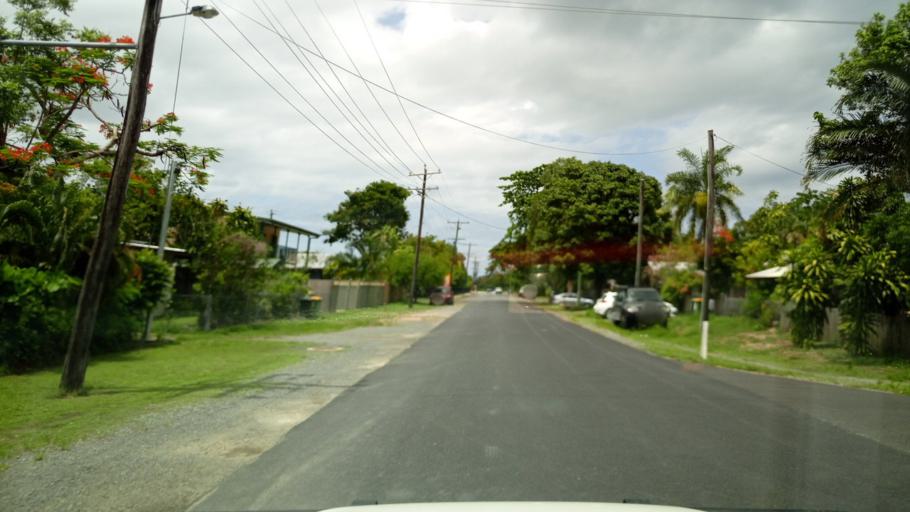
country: AU
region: Queensland
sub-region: Cairns
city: Redlynch
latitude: -16.8549
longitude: 145.7455
